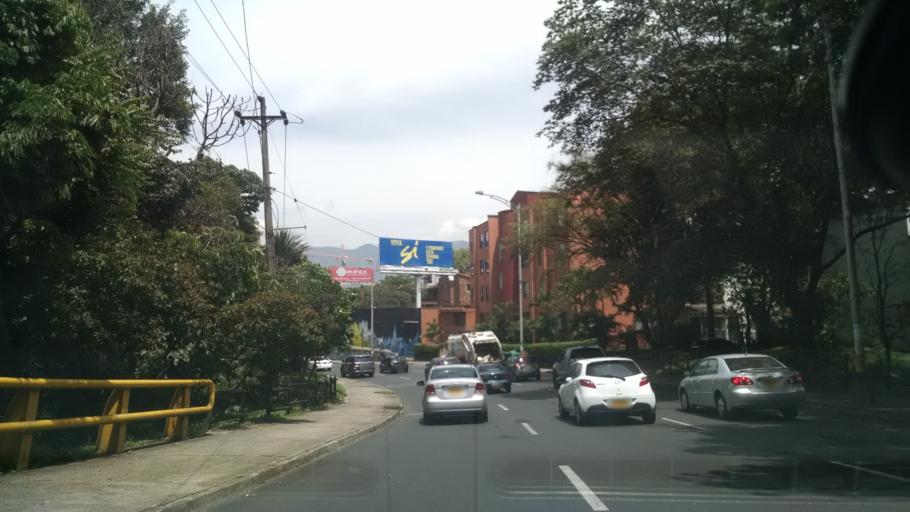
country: CO
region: Antioquia
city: Itagui
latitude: 6.2127
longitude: -75.5728
